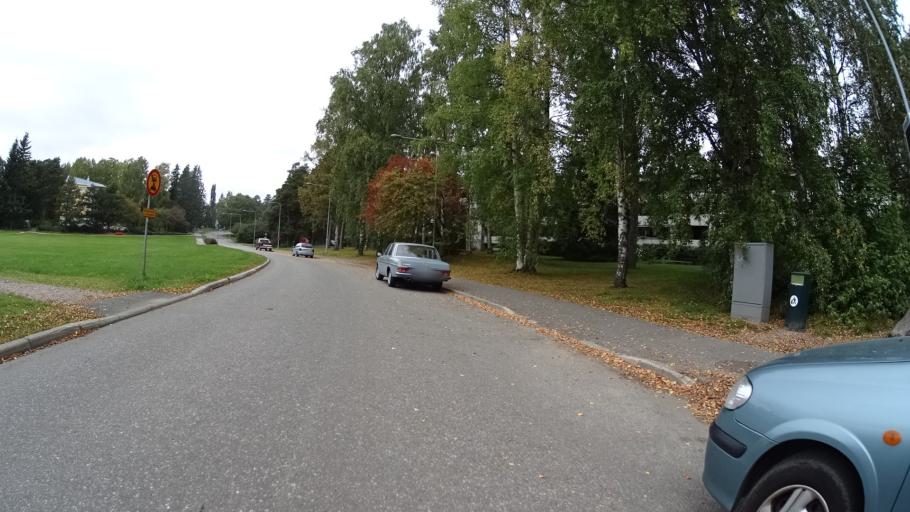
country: FI
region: Uusimaa
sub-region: Helsinki
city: Otaniemi
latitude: 60.1776
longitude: 24.8244
